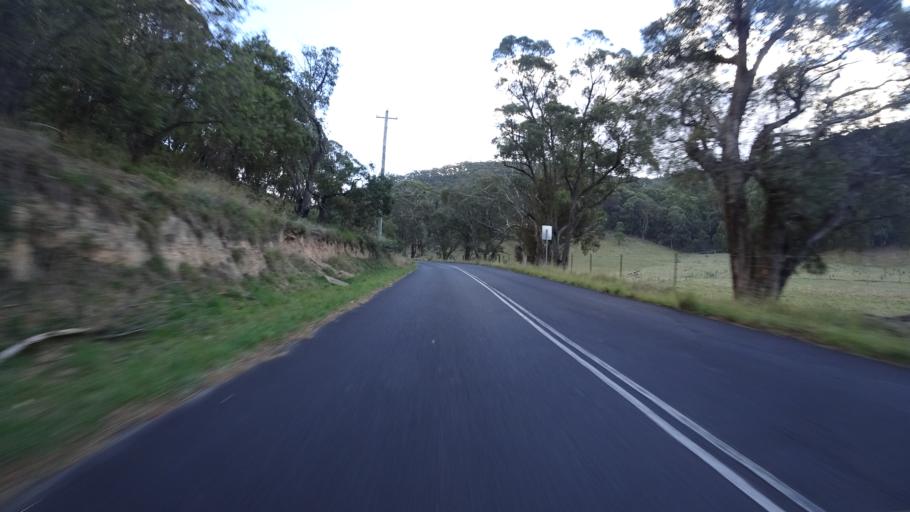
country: AU
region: New South Wales
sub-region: Lithgow
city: Lithgow
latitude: -33.4924
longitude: 150.1746
